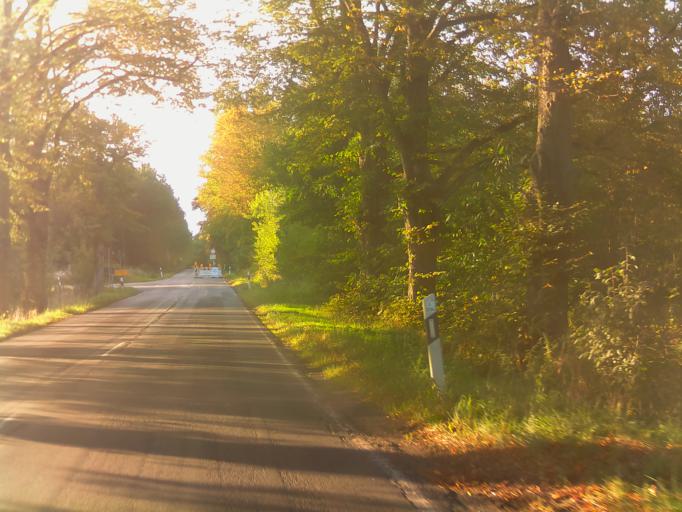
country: DE
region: Hesse
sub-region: Regierungsbezirk Darmstadt
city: Wachtersbach
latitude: 50.2913
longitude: 9.2430
